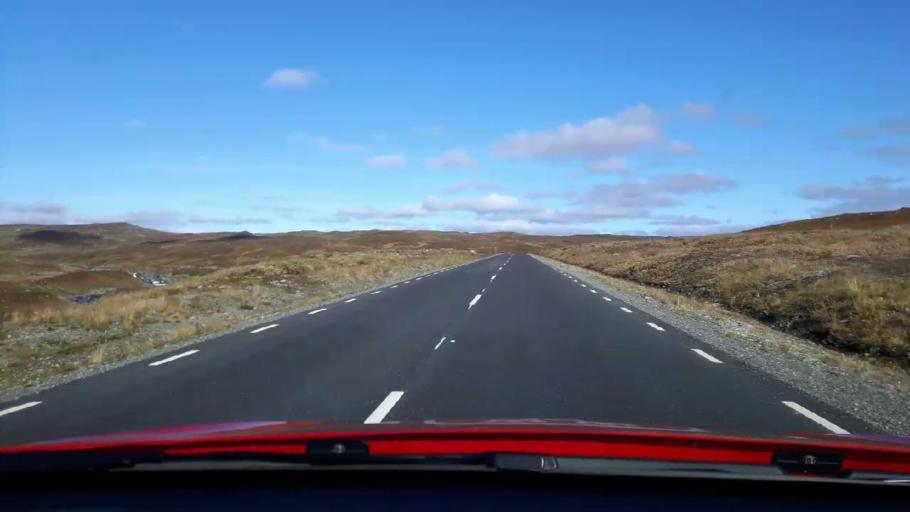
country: NO
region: Nordland
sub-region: Hattfjelldal
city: Hattfjelldal
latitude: 65.0423
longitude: 14.3295
